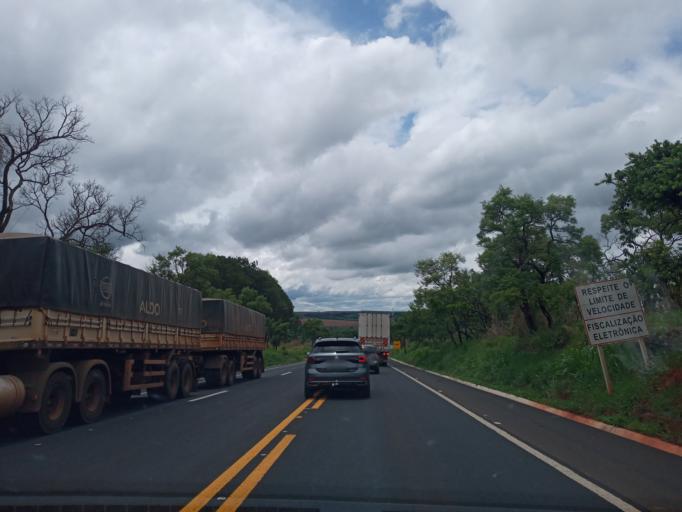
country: BR
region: Minas Gerais
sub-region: Uberaba
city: Uberaba
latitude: -19.2878
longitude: -47.6174
